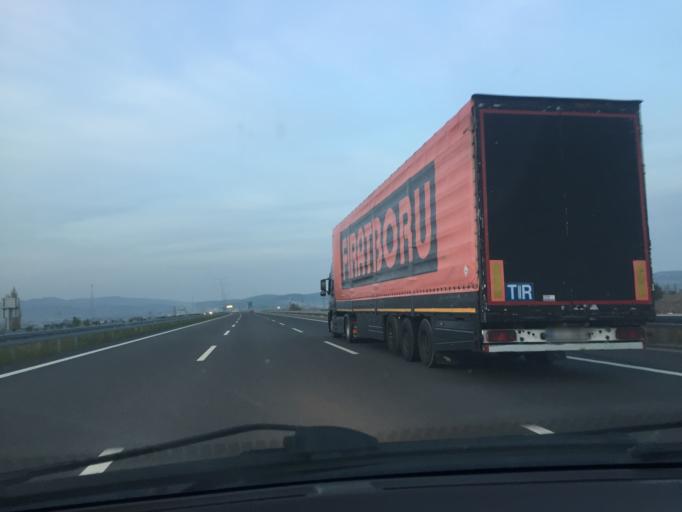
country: TR
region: Manisa
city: Halitpasa
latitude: 38.7544
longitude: 27.6602
